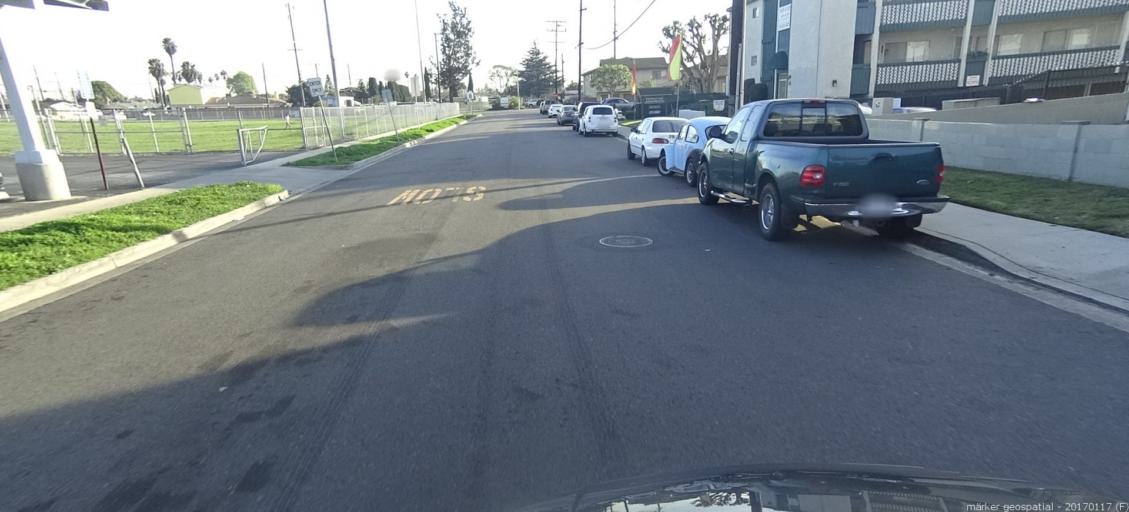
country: US
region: California
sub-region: Orange County
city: Midway City
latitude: 33.7387
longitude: -117.9863
